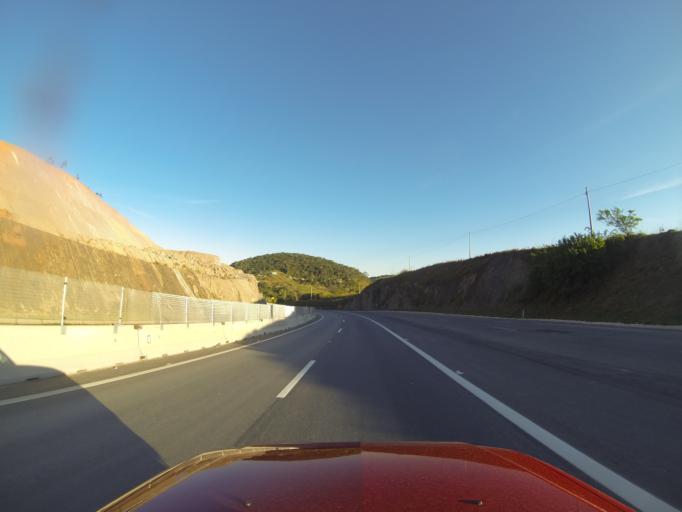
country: BR
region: Sao Paulo
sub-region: Santa Branca
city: Santa Branca
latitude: -23.3490
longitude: -45.7088
